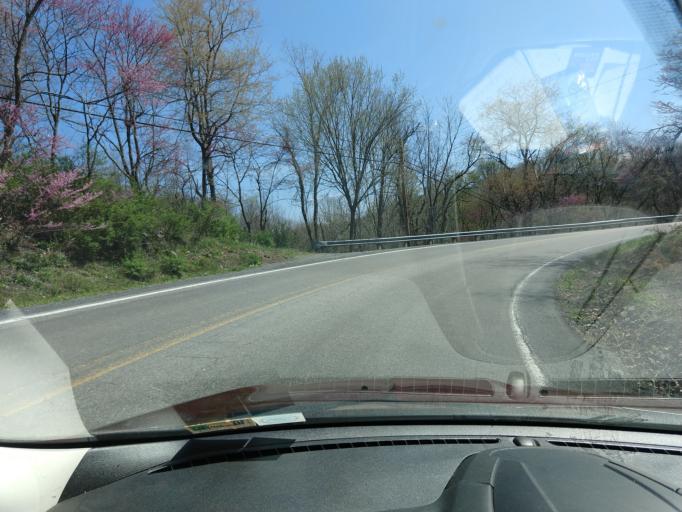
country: US
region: West Virginia
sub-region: Greenbrier County
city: Ronceverte
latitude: 37.7565
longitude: -80.5337
